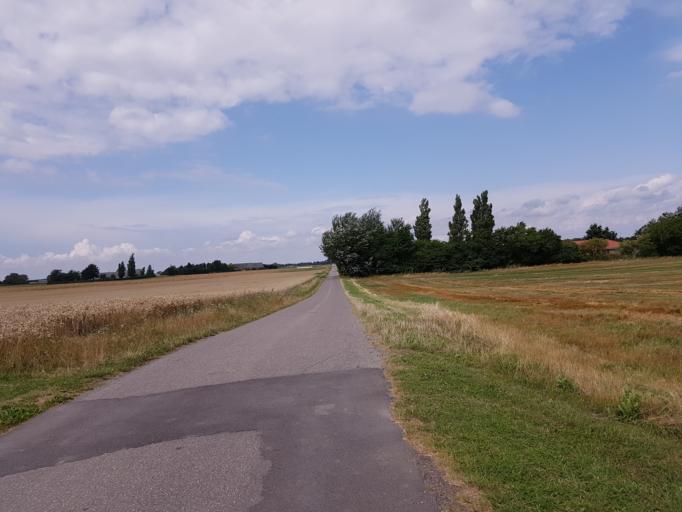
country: DK
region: Zealand
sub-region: Guldborgsund Kommune
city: Nykobing Falster
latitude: 54.5834
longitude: 11.9582
